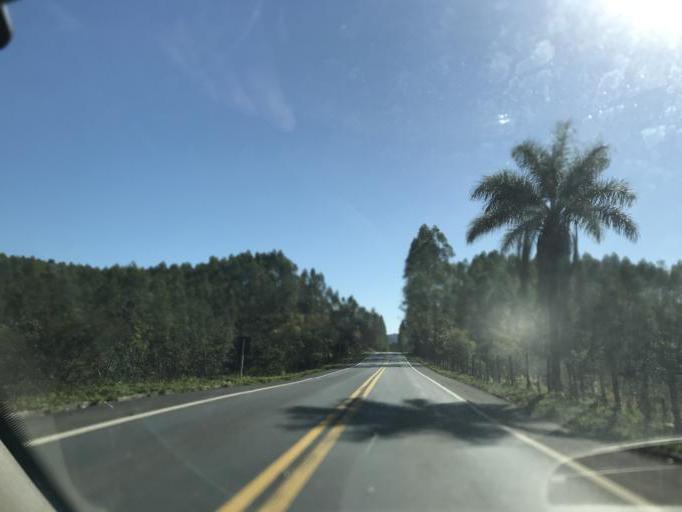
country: BR
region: Minas Gerais
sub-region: Bambui
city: Bambui
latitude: -19.8238
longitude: -46.0118
